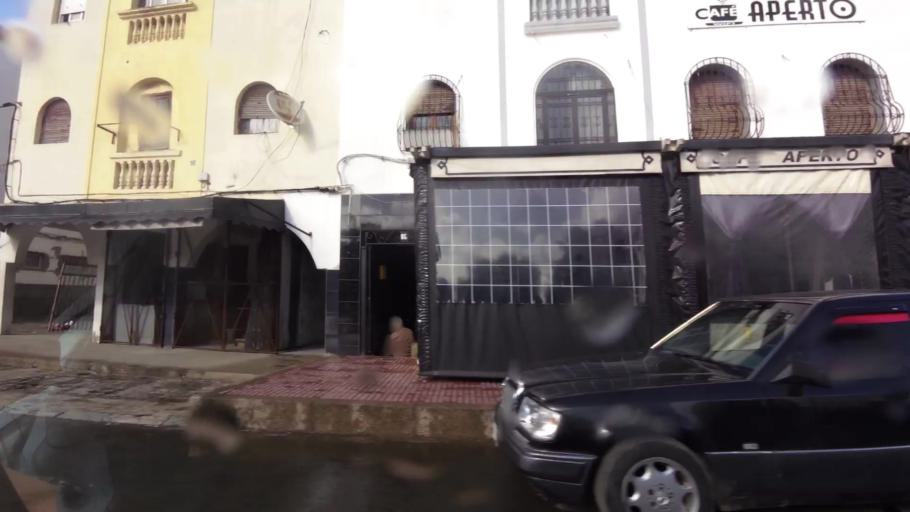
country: MA
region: Grand Casablanca
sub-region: Casablanca
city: Casablanca
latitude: 33.5578
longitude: -7.6923
